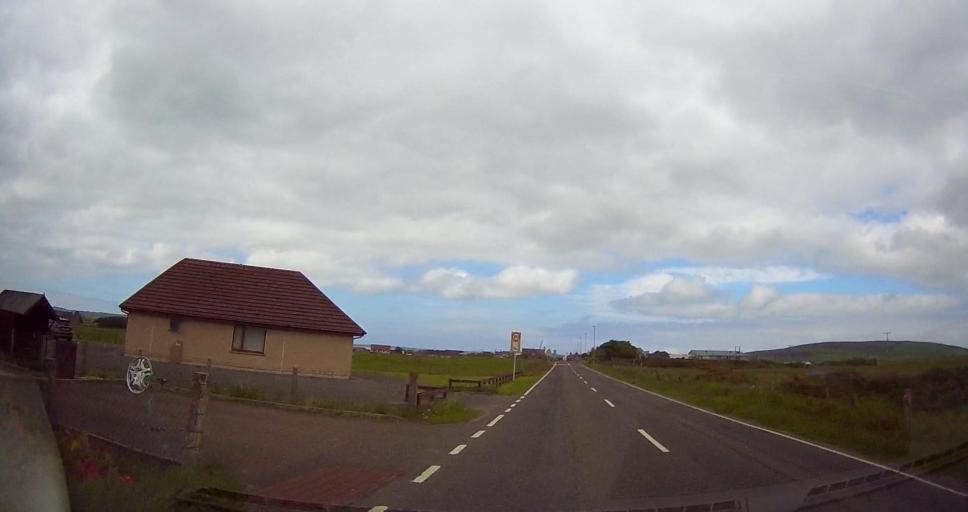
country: GB
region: Scotland
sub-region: Orkney Islands
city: Stromness
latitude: 59.0640
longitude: -3.2251
